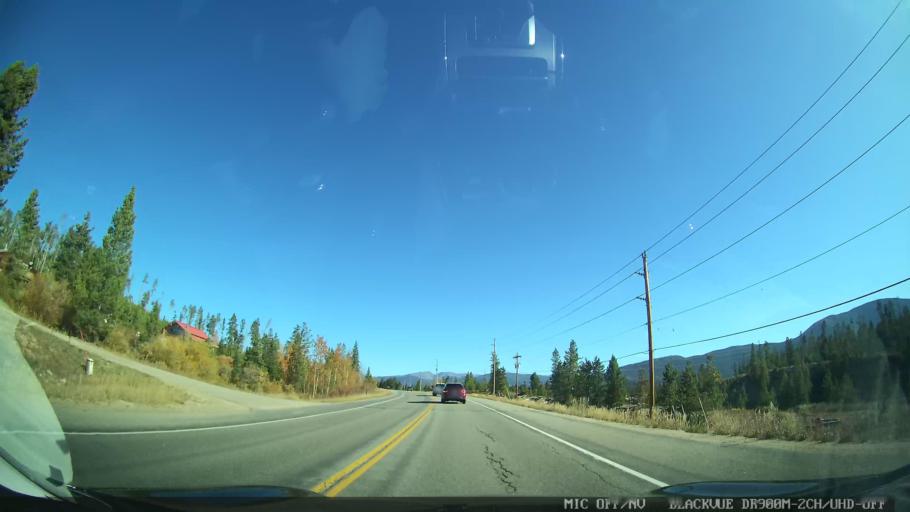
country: US
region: Colorado
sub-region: Grand County
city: Granby
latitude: 40.2037
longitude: -105.8616
